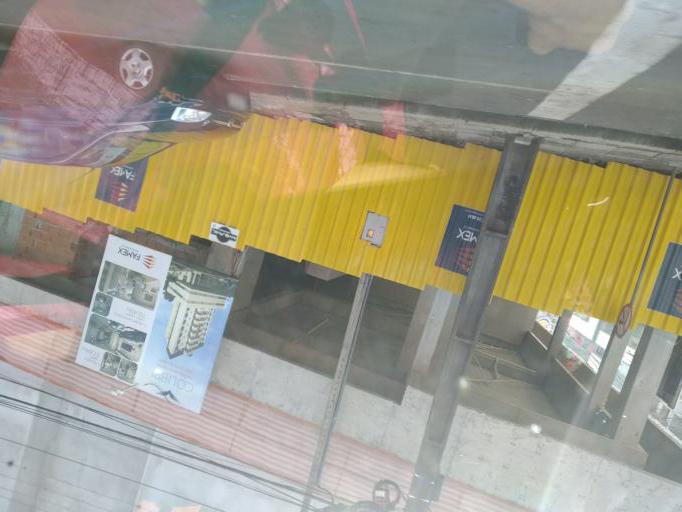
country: BR
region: Parana
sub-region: Pato Branco
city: Pato Branco
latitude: -26.2300
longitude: -52.6725
